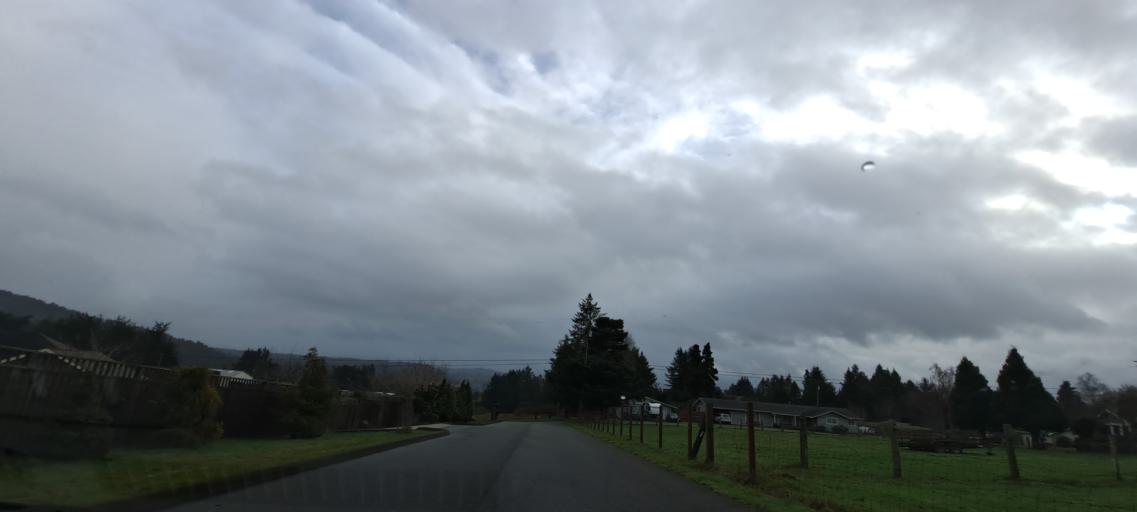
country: US
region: California
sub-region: Humboldt County
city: Fortuna
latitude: 40.6053
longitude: -124.1354
